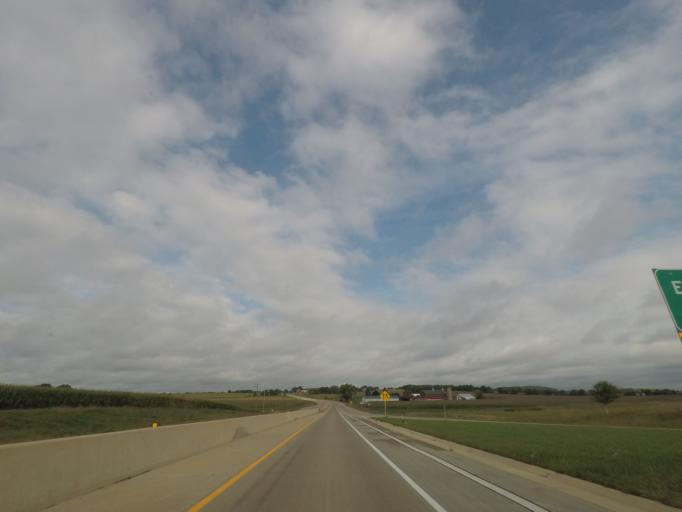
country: US
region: Wisconsin
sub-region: Dane County
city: Deerfield
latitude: 43.0290
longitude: -89.0803
